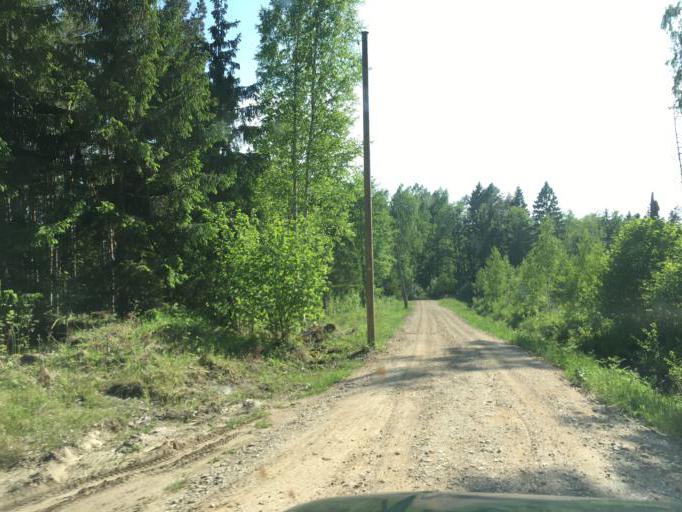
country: LV
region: Dundaga
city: Dundaga
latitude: 57.6052
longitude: 22.5115
